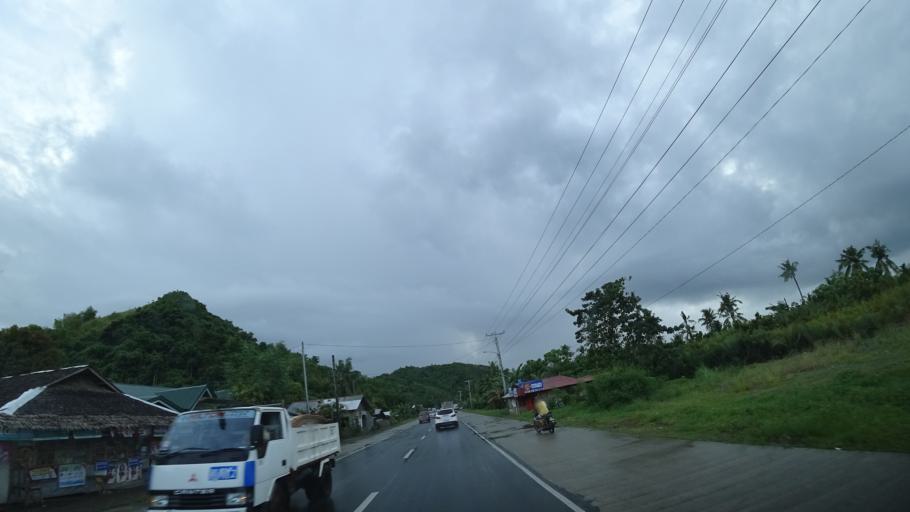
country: PH
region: Eastern Visayas
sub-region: Province of Leyte
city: Kabuynan
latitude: 11.0872
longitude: 125.0230
